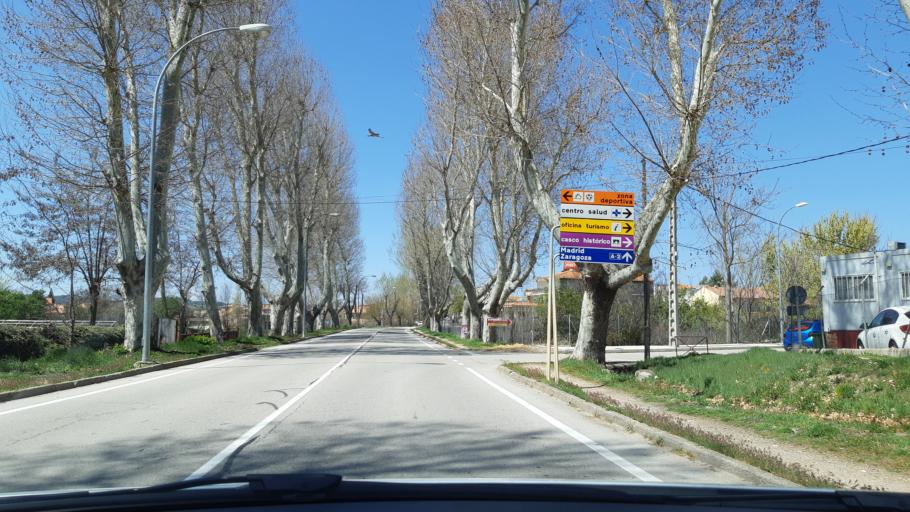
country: ES
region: Castille-La Mancha
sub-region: Provincia de Guadalajara
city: Cifuentes
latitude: 40.7830
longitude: -2.6245
